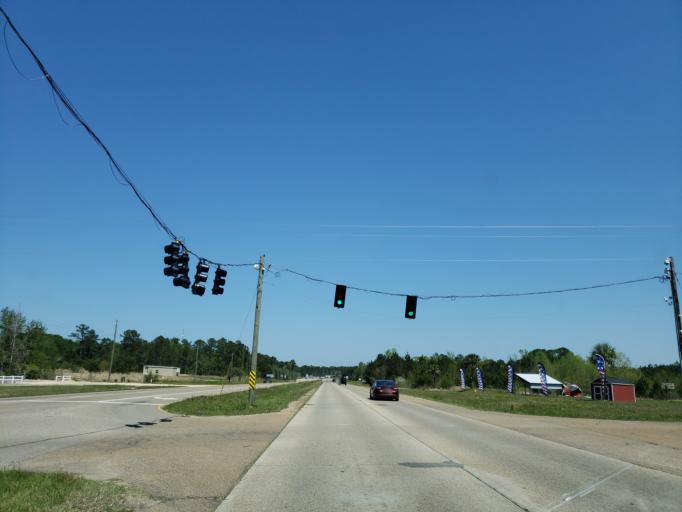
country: US
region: Mississippi
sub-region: Harrison County
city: Lyman
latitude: 30.5174
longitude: -89.1084
